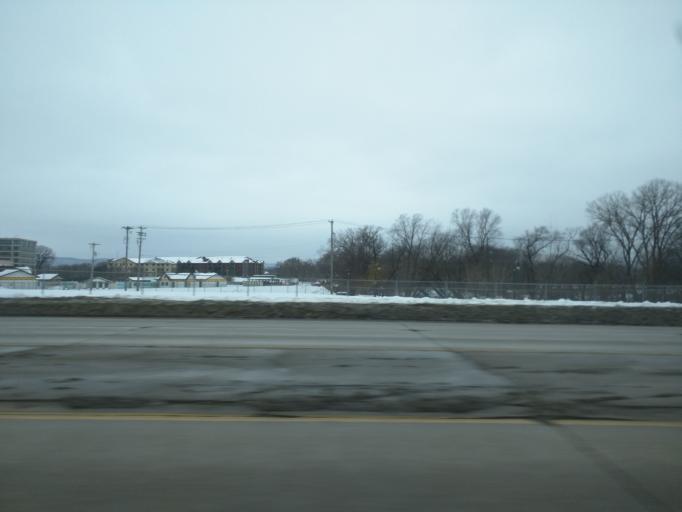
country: US
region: Wisconsin
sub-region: La Crosse County
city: La Crosse
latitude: 43.8190
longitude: -91.2490
